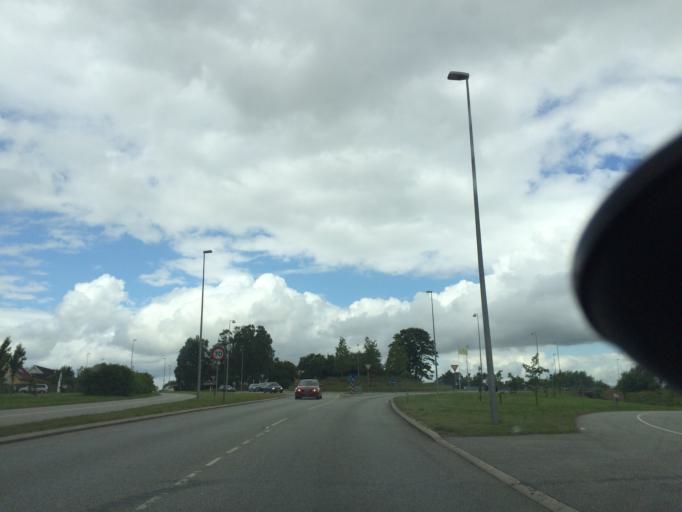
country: DK
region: Central Jutland
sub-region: Arhus Kommune
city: Kolt
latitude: 56.1523
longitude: 10.0767
